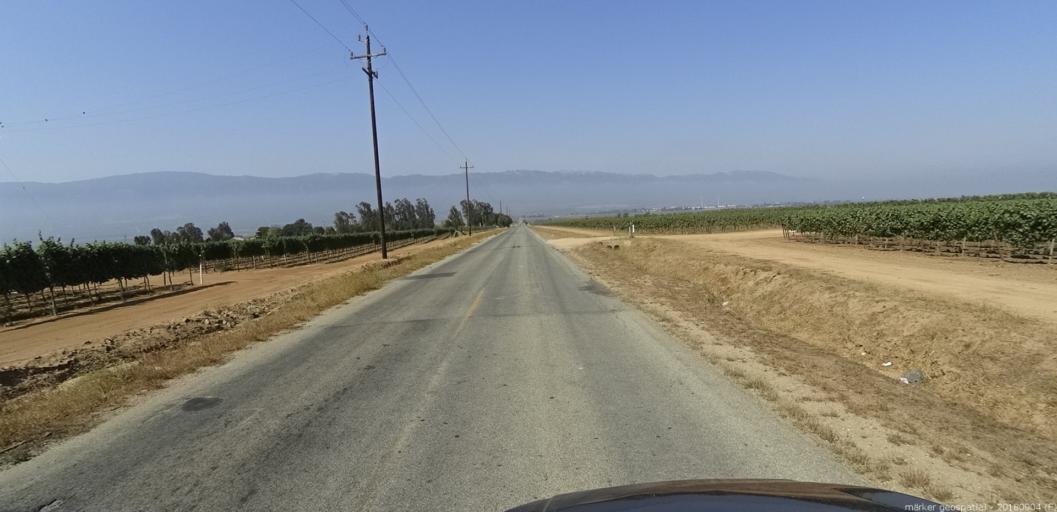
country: US
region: California
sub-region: Monterey County
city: Gonzales
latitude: 36.5011
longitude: -121.3981
